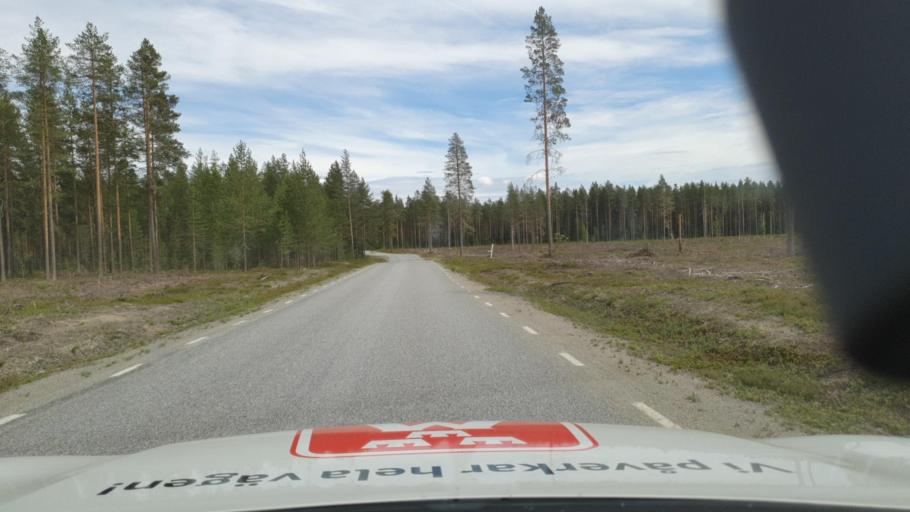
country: SE
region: Vaesterbotten
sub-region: Skelleftea Kommun
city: Burtraesk
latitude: 64.5017
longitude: 20.8393
